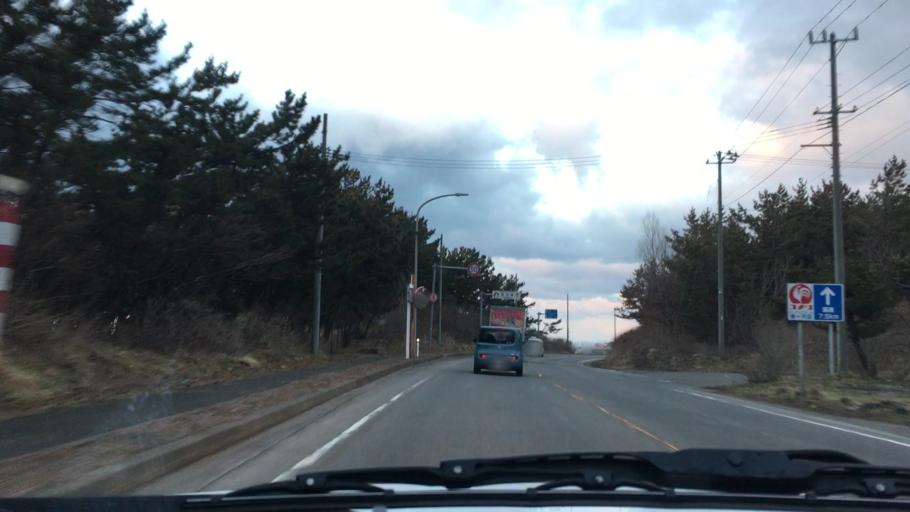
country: JP
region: Aomori
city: Shimokizukuri
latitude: 40.7580
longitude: 140.1550
